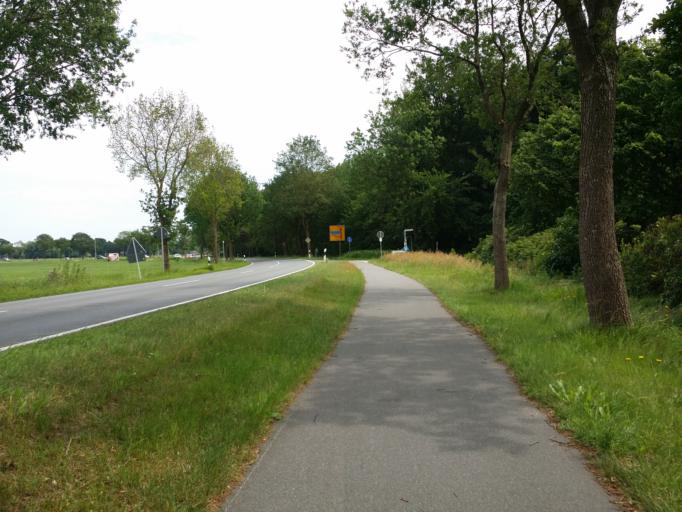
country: DE
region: Lower Saxony
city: Wiefelstede
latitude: 53.2458
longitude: 8.1299
